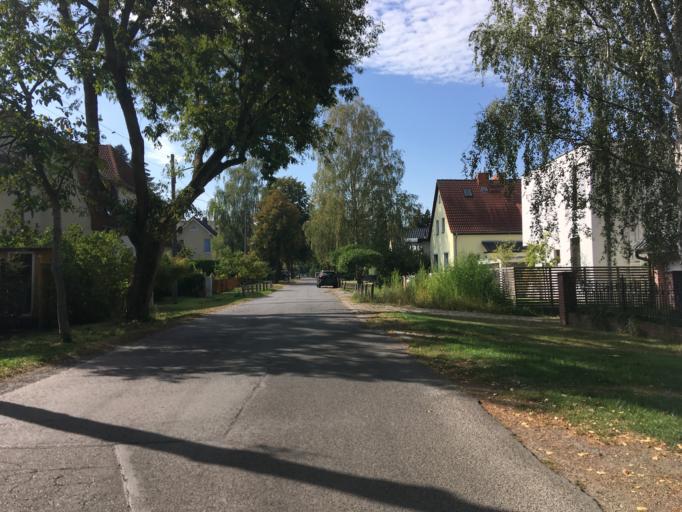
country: DE
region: Berlin
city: Mahlsdorf
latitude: 52.5173
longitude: 13.6282
